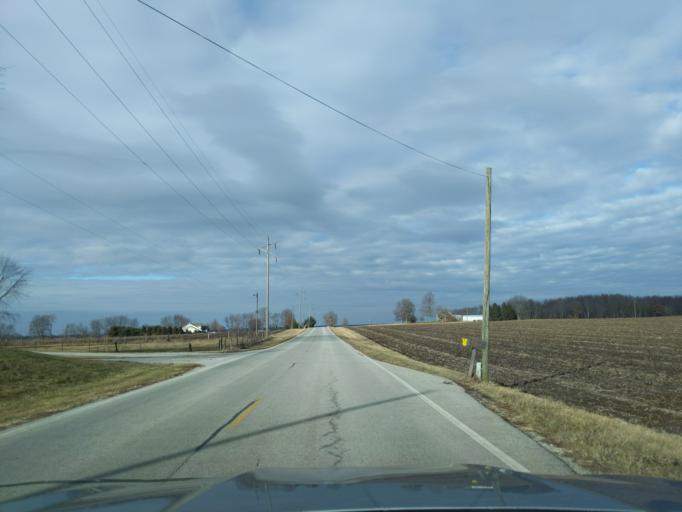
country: US
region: Indiana
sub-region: Tippecanoe County
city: Shadeland
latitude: 40.3484
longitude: -86.9755
